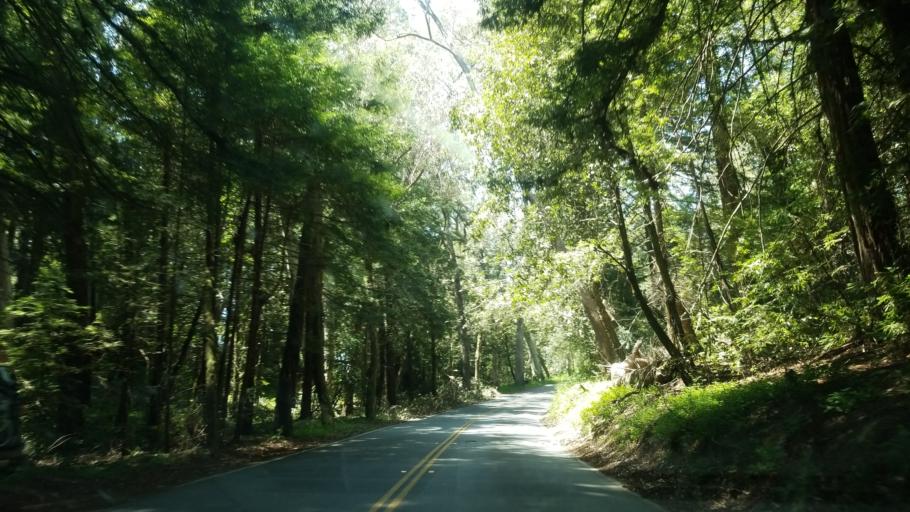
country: US
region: California
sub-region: Santa Cruz County
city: Interlaken
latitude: 37.0055
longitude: -121.7105
